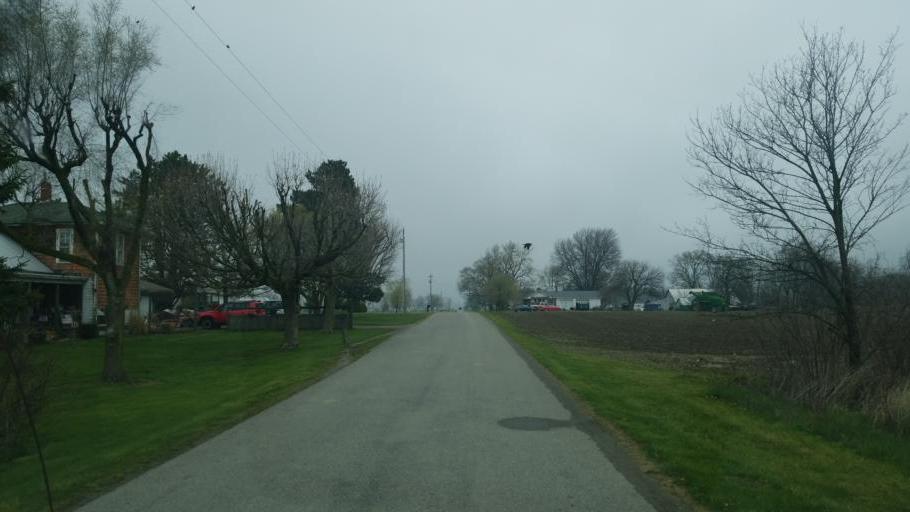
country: US
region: Ohio
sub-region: Logan County
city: Northwood
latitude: 40.5281
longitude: -83.6625
